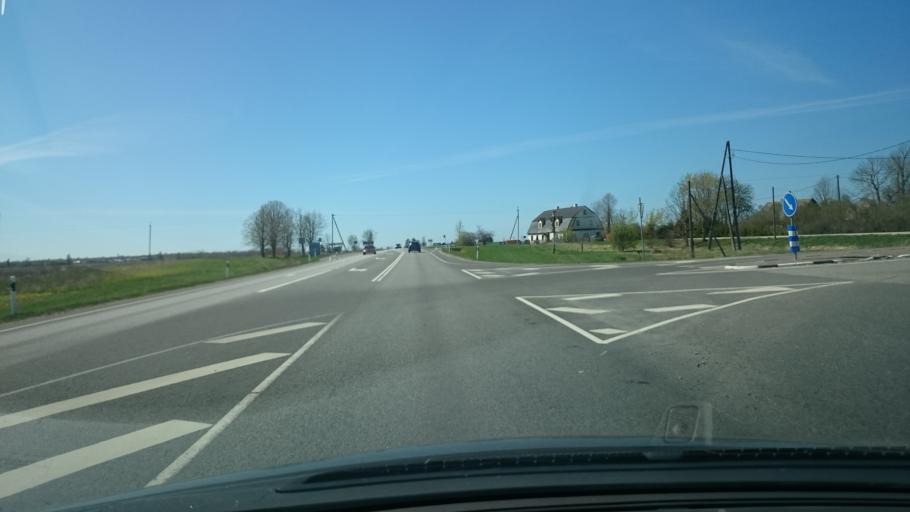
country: EE
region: Ida-Virumaa
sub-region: Narva-Joesuu linn
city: Narva-Joesuu
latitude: 59.4009
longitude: 28.0654
